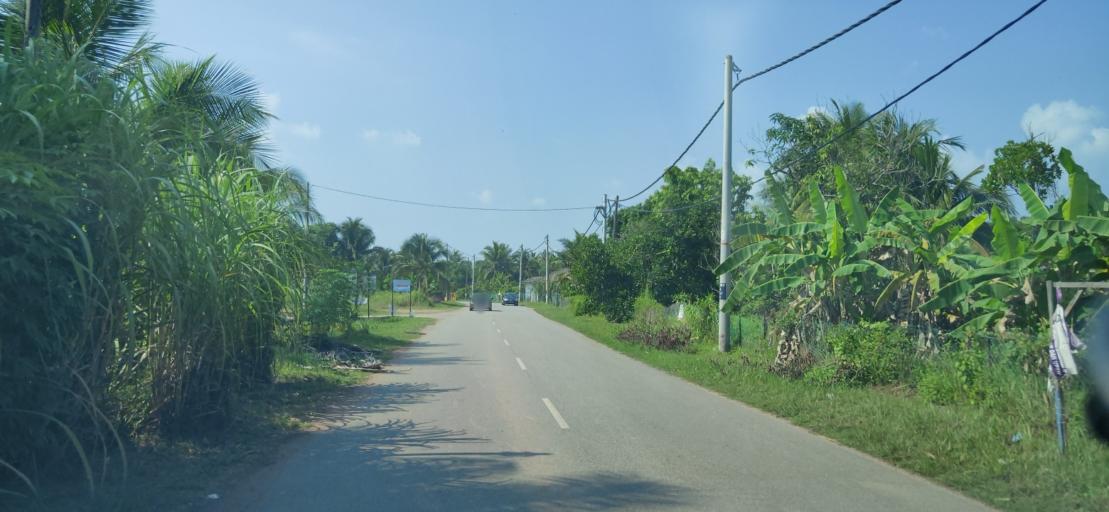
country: MY
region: Kedah
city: Sungai Petani
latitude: 5.6564
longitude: 100.4617
